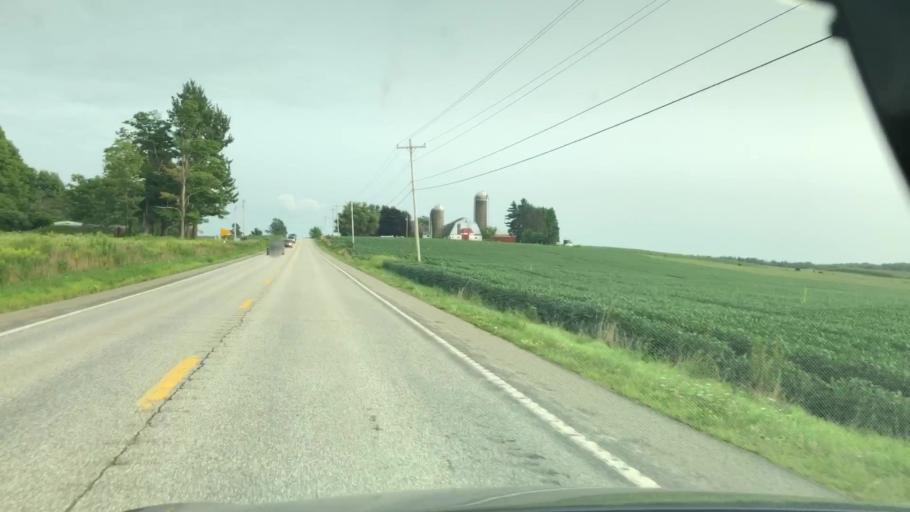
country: US
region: Pennsylvania
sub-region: Erie County
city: Union City
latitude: 41.8627
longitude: -79.8326
